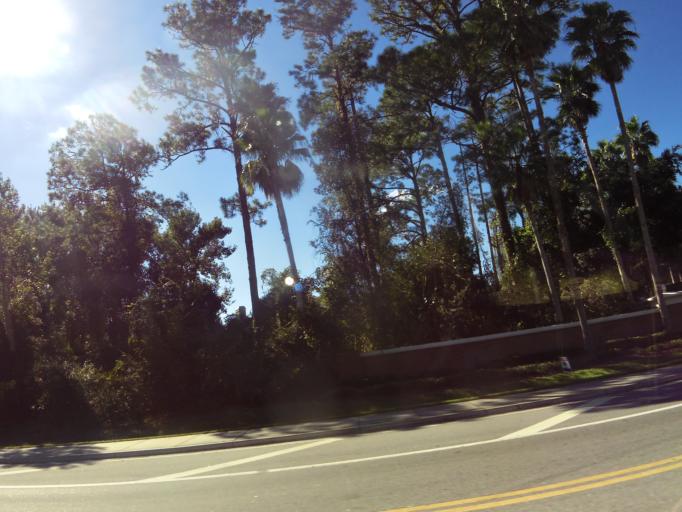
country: US
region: Florida
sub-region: Saint Johns County
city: Palm Valley
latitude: 30.1447
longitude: -81.3771
